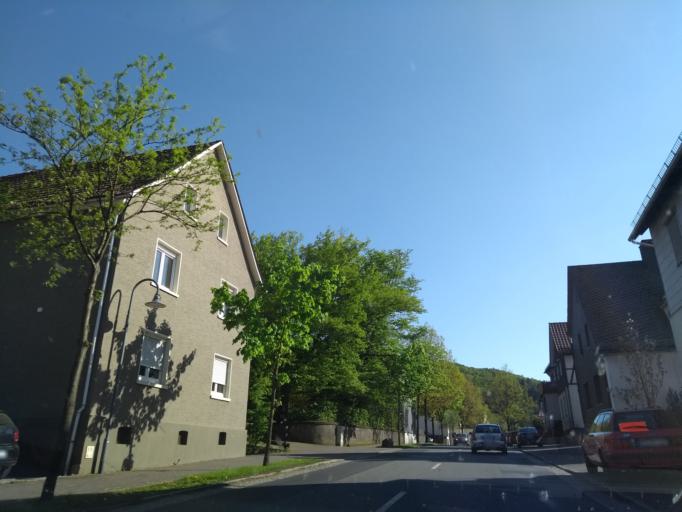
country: DE
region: Hesse
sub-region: Regierungsbezirk Giessen
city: Breidenbach
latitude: 50.9153
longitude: 8.4697
